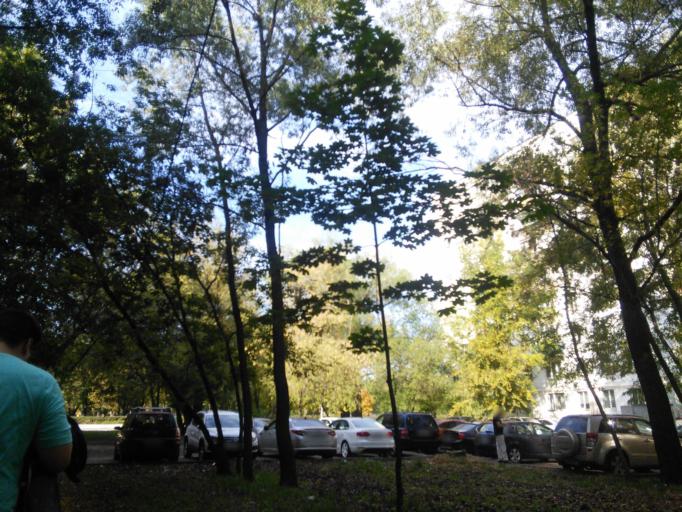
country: RU
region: Moscow
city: Mar'ina Roshcha
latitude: 55.8116
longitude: 37.5878
